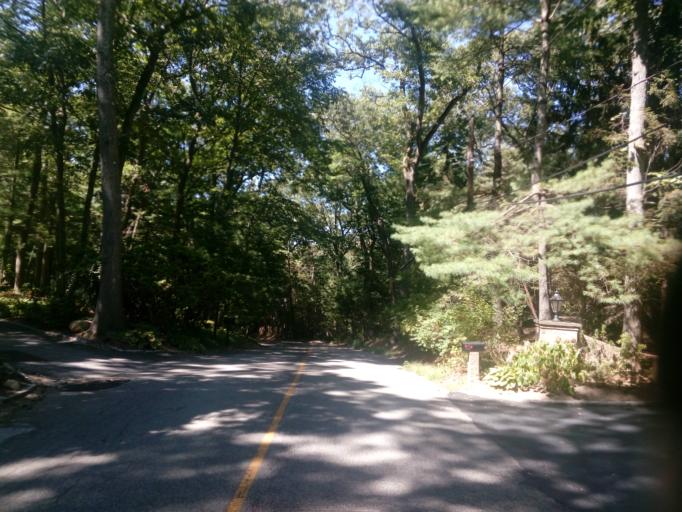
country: US
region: New York
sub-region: Nassau County
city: Upper Brookville
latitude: 40.8444
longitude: -73.5684
